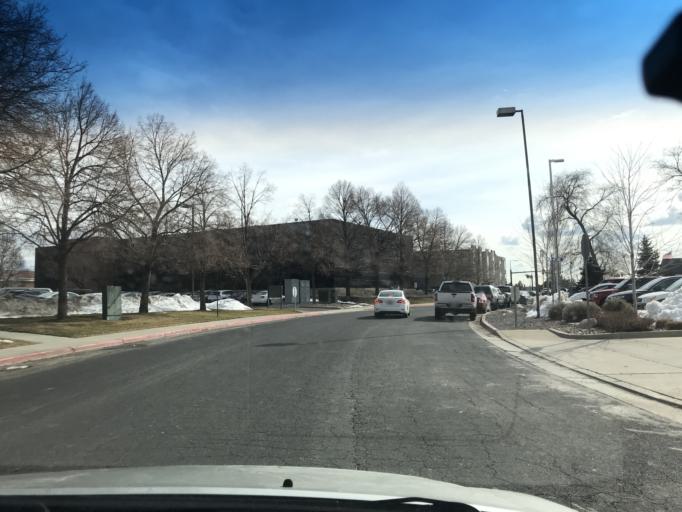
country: US
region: Utah
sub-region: Salt Lake County
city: Salt Lake City
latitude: 40.7733
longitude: -111.9473
